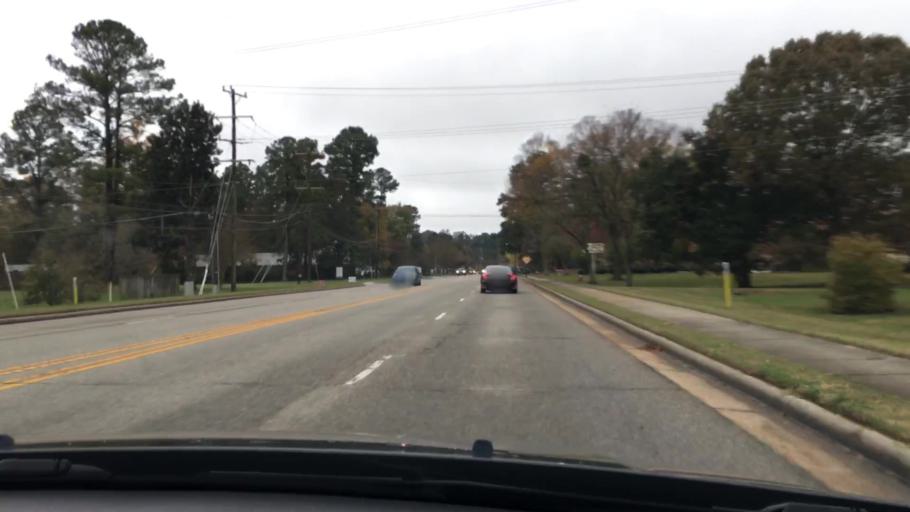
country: US
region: Virginia
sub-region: City of Williamsburg
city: Williamsburg
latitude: 37.2851
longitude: -76.6872
